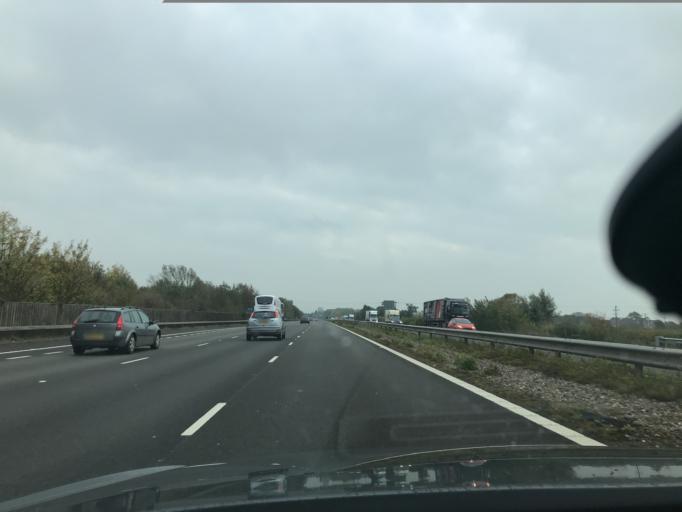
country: GB
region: England
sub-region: Oxfordshire
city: Chalgrove
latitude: 51.7293
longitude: -1.0686
